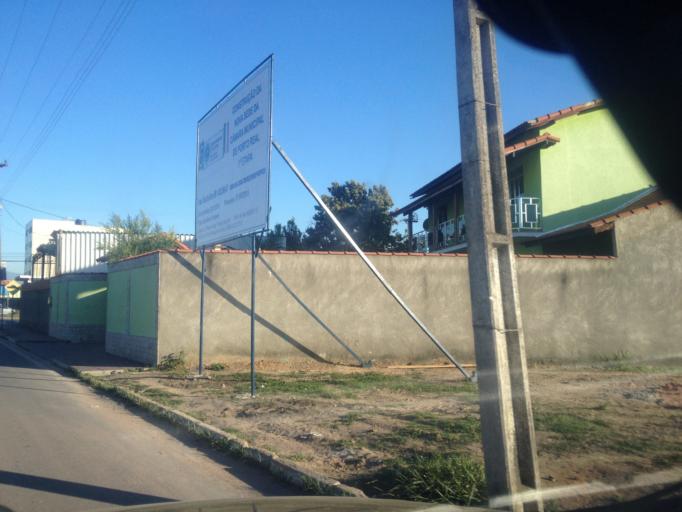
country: BR
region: Rio de Janeiro
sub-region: Porto Real
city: Porto Real
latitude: -22.4178
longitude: -44.3022
